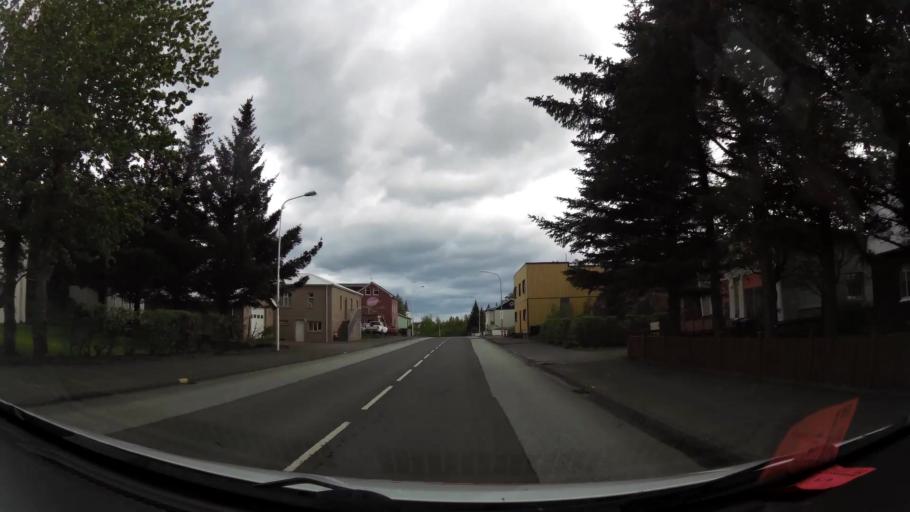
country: IS
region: West
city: Borgarnes
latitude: 64.5408
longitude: -21.9173
